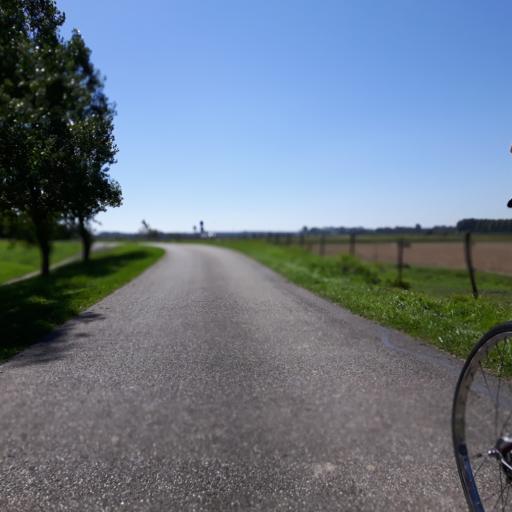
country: NL
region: Zeeland
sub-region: Gemeente Noord-Beveland
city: Kamperland
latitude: 51.5830
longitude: 3.7894
